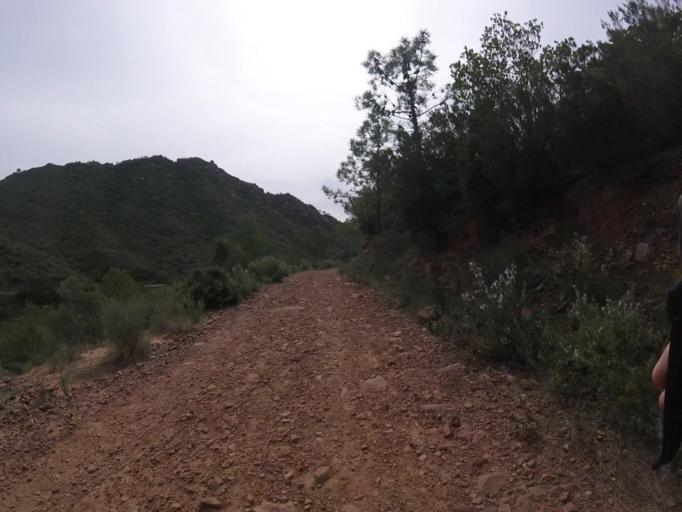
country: ES
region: Valencia
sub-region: Provincia de Castello
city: Benicassim
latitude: 40.0698
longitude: 0.0381
